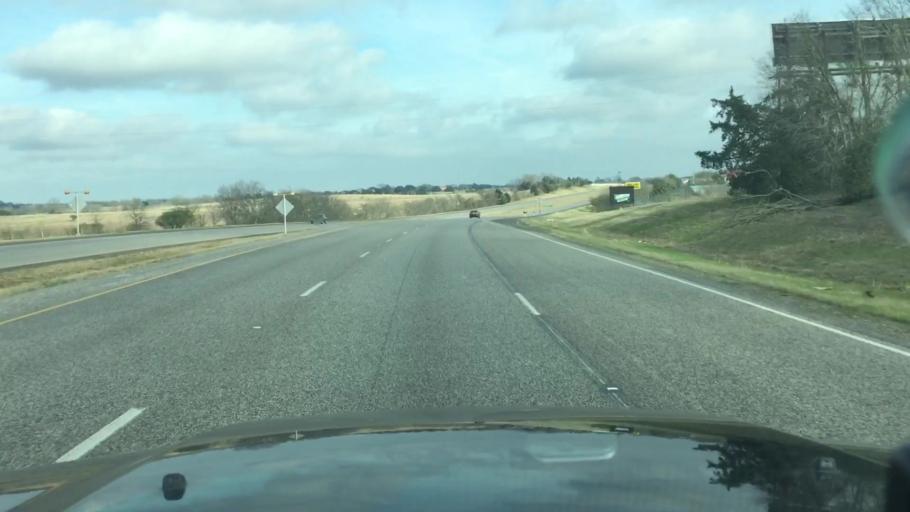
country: US
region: Texas
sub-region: Washington County
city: Brenham
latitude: 30.1355
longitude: -96.2546
